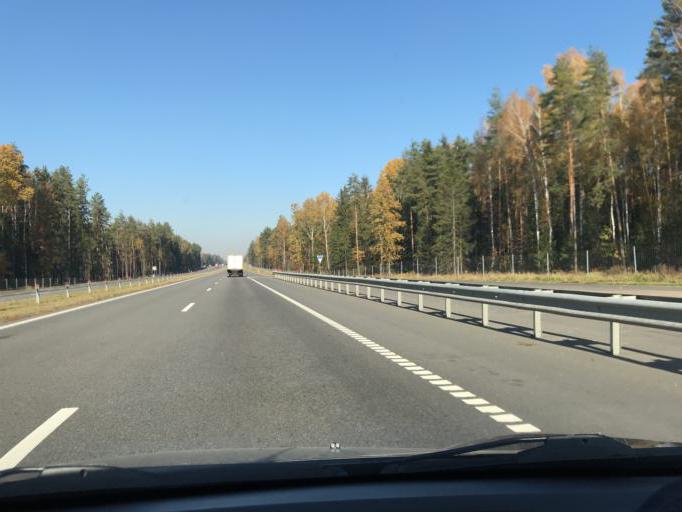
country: BY
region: Mogilev
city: Babruysk
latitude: 53.2029
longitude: 29.3484
